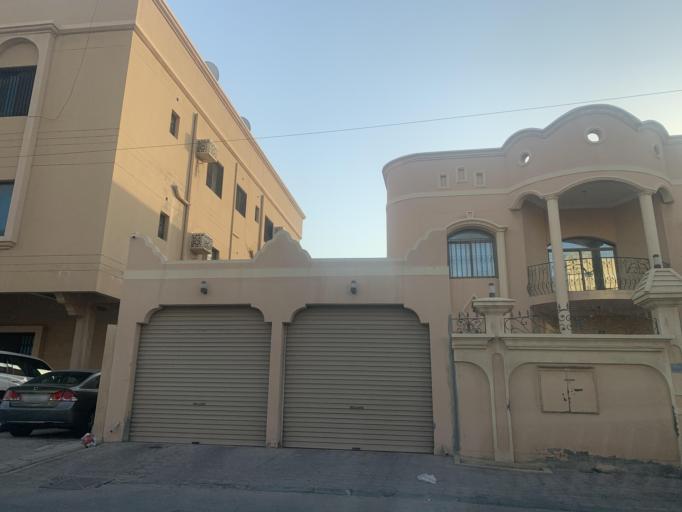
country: BH
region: Manama
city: Jidd Hafs
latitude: 26.2133
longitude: 50.5304
